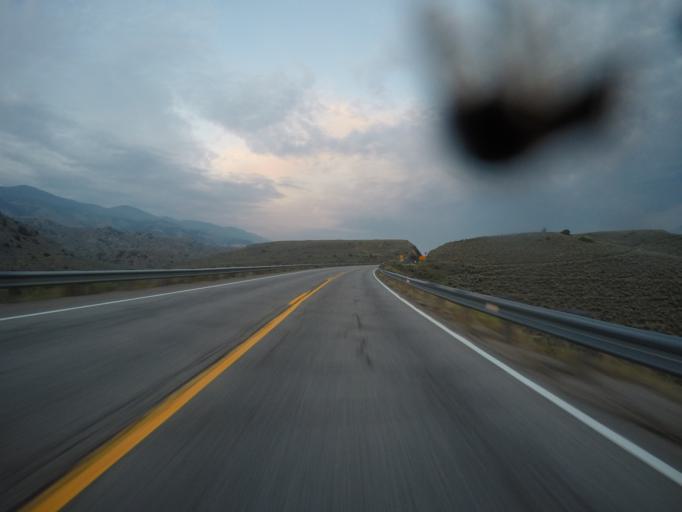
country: US
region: Colorado
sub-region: Grand County
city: Kremmling
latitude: 39.8699
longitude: -106.2640
